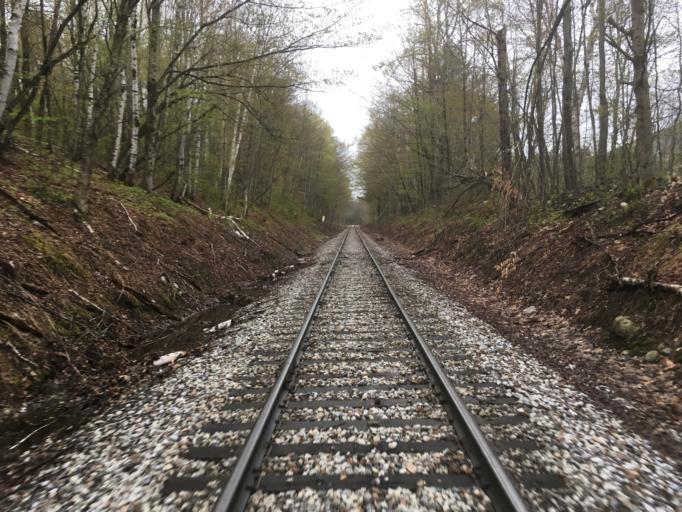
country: US
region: Vermont
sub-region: Rutland County
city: Rutland
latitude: 43.4855
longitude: -72.8771
